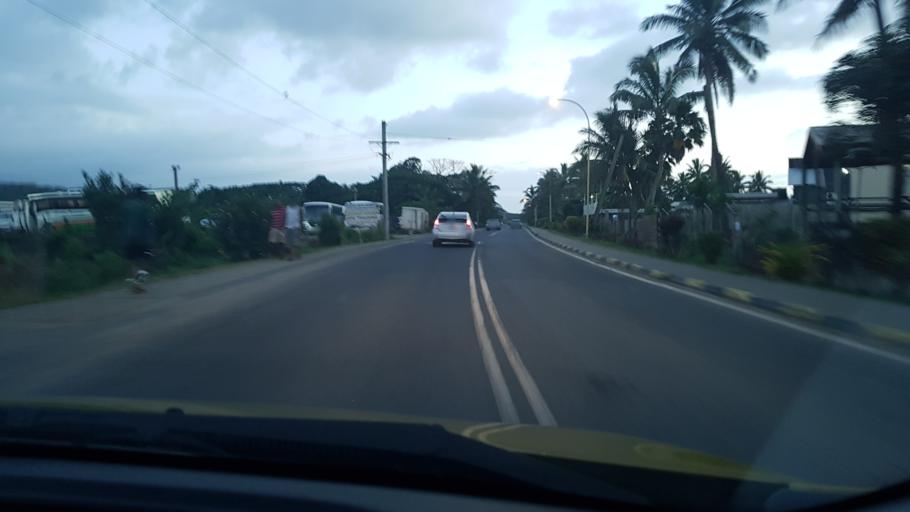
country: FJ
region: Western
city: Nadi
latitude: -18.1426
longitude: 177.5121
